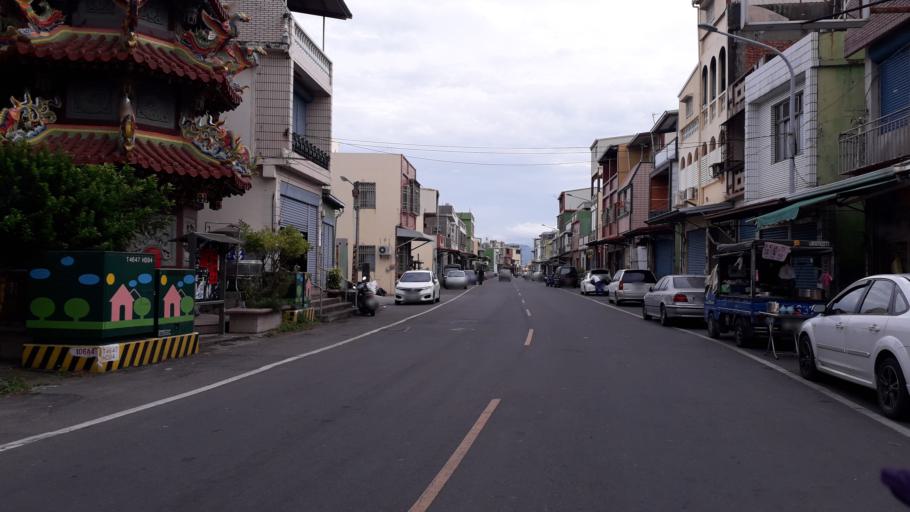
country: TW
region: Taiwan
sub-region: Pingtung
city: Pingtung
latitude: 22.3615
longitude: 120.5961
